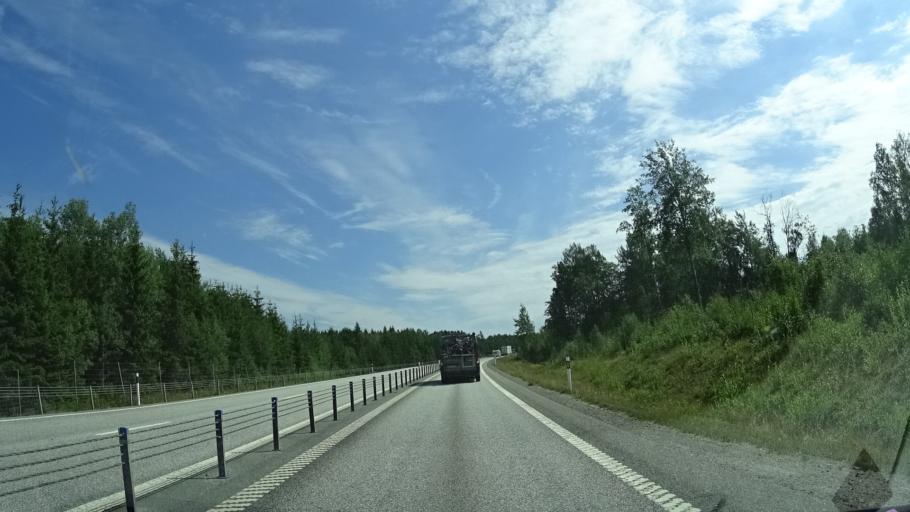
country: SE
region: OErebro
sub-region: Karlskoga Kommun
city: Karlskoga
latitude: 59.3268
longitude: 14.4349
